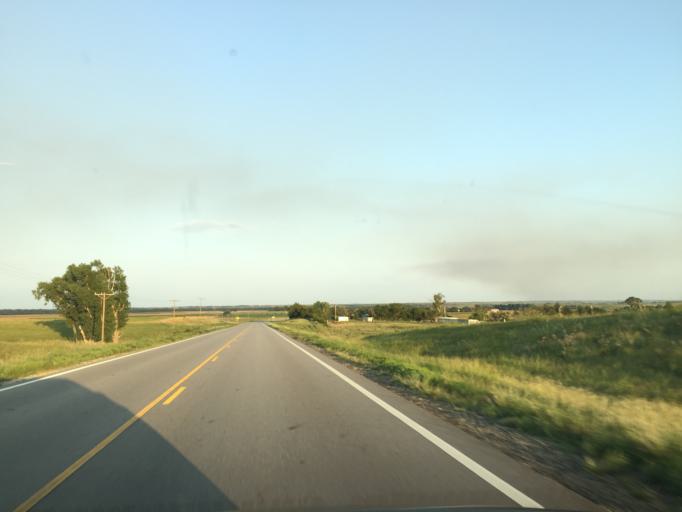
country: US
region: Kansas
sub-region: Ellsworth County
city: Ellsworth
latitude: 38.6965
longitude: -98.2098
